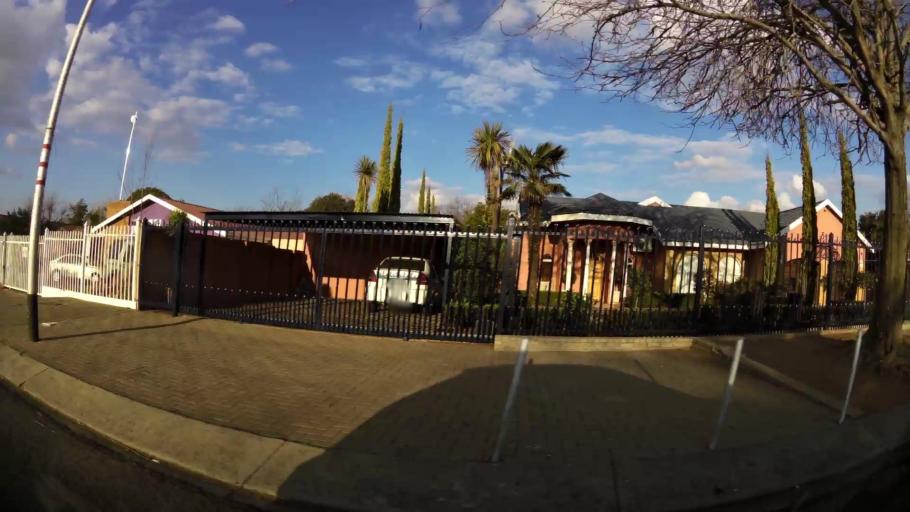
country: ZA
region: Orange Free State
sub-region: Mangaung Metropolitan Municipality
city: Bloemfontein
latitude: -29.1520
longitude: 26.1851
